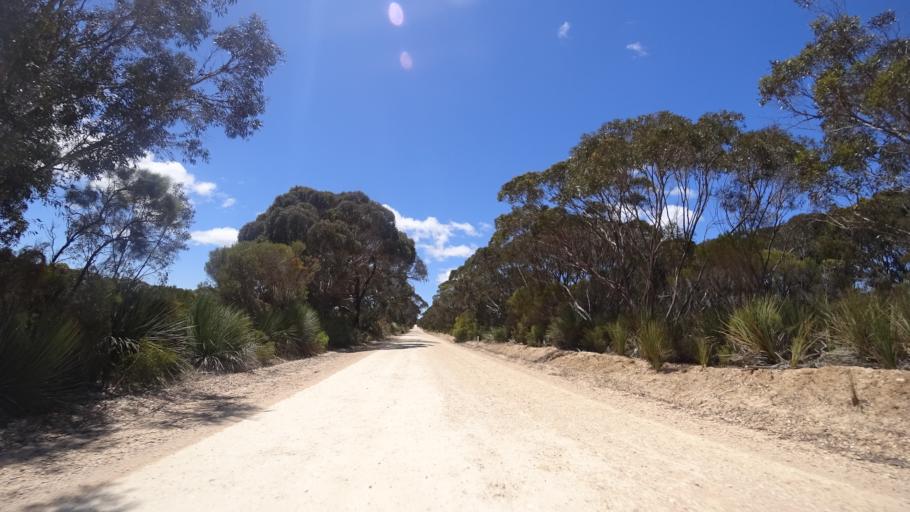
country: AU
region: South Australia
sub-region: Kangaroo Island
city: Kingscote
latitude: -35.8263
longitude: 138.0106
